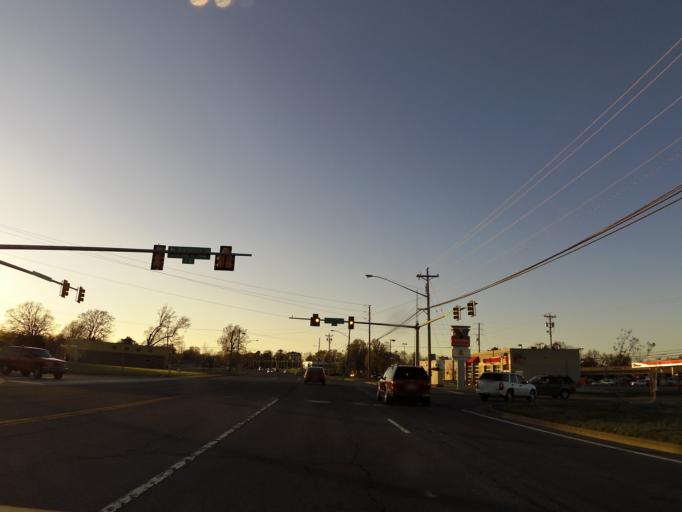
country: US
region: Tennessee
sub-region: Robertson County
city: Springfield
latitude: 36.4862
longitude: -86.8637
